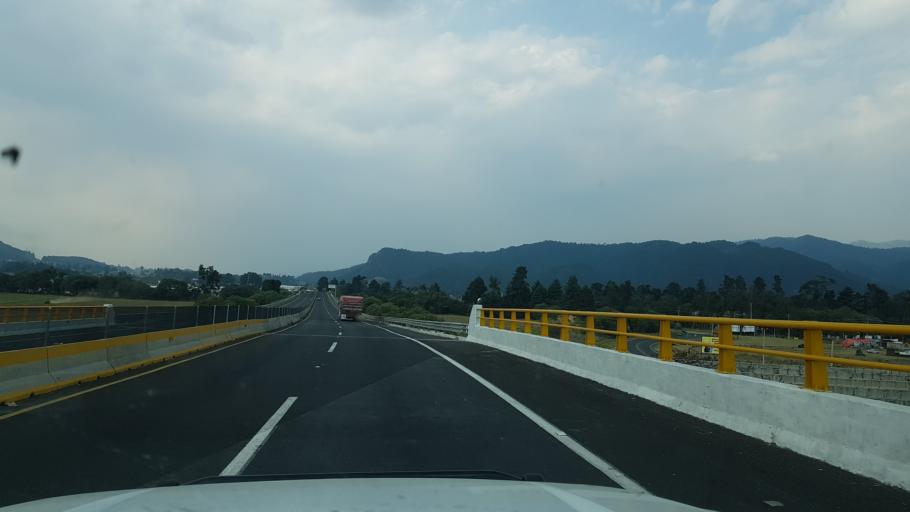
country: MX
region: Mexico
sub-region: Ayapango
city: La Colonia
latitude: 19.1397
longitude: -98.7761
